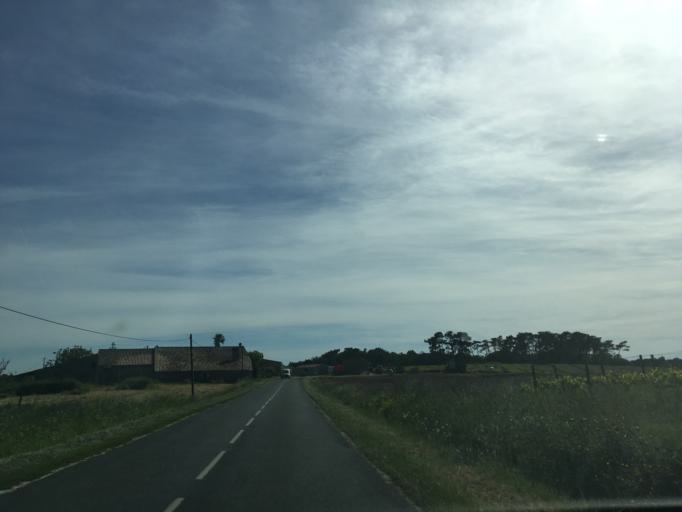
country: FR
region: Poitou-Charentes
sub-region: Departement de la Charente-Maritime
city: Mirambeau
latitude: 45.3367
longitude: -0.5914
